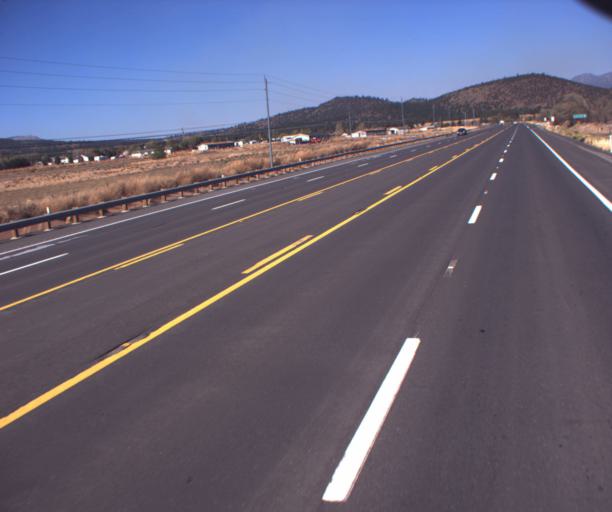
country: US
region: Arizona
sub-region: Coconino County
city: Flagstaff
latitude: 35.3188
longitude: -111.5427
